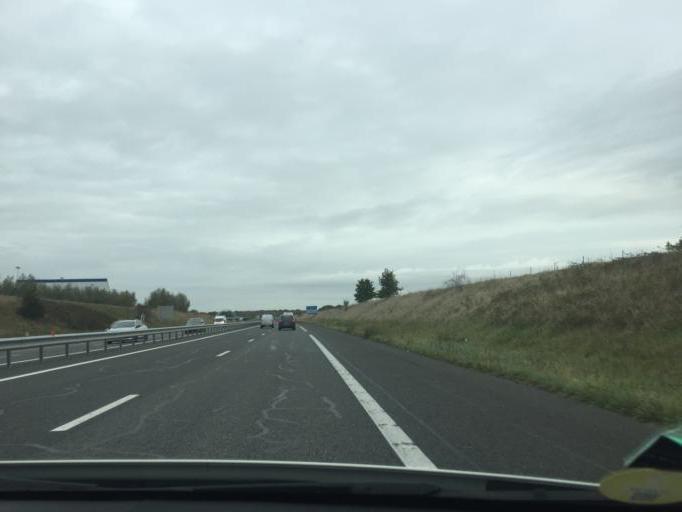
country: FR
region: Bourgogne
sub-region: Departement de l'Yonne
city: Egriselles-le-Bocage
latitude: 48.1583
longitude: 3.1738
